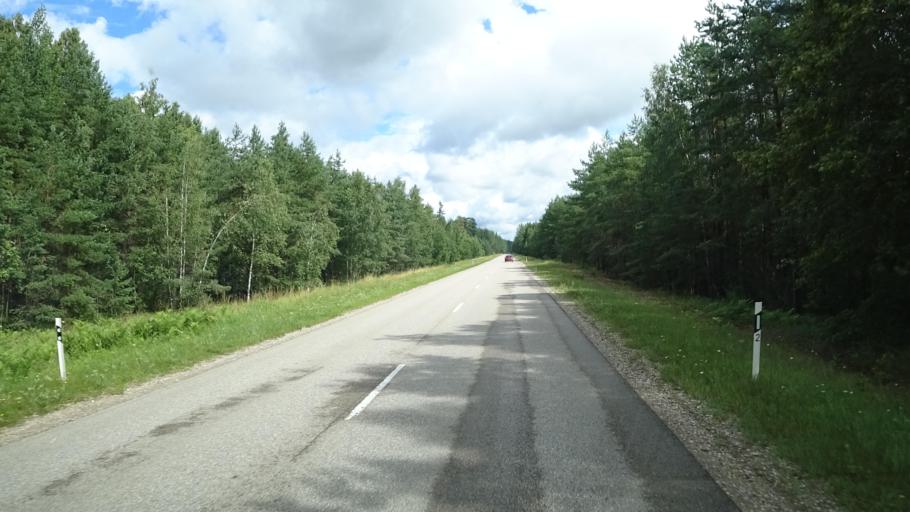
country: LV
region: Pavilostas
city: Pavilosta
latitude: 56.7205
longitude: 21.1875
